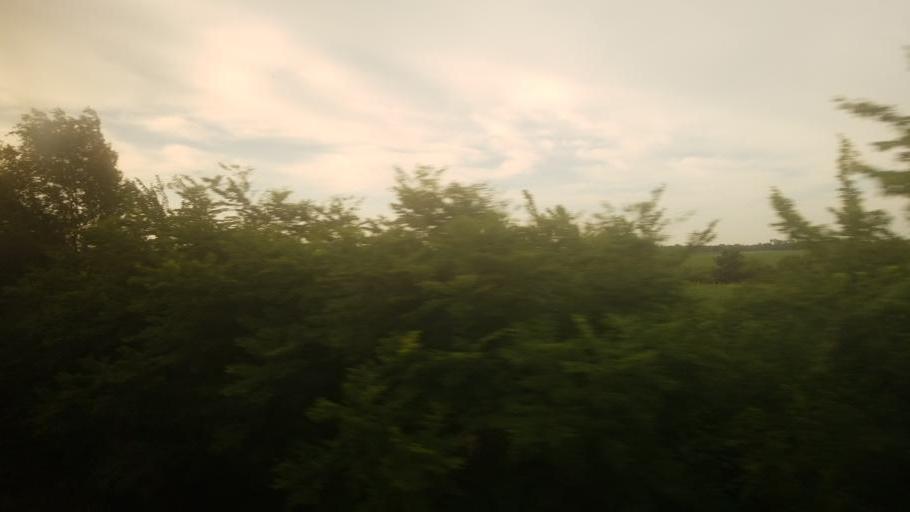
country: US
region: Kansas
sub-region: Osage County
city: Osage City
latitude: 38.5180
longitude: -95.9545
